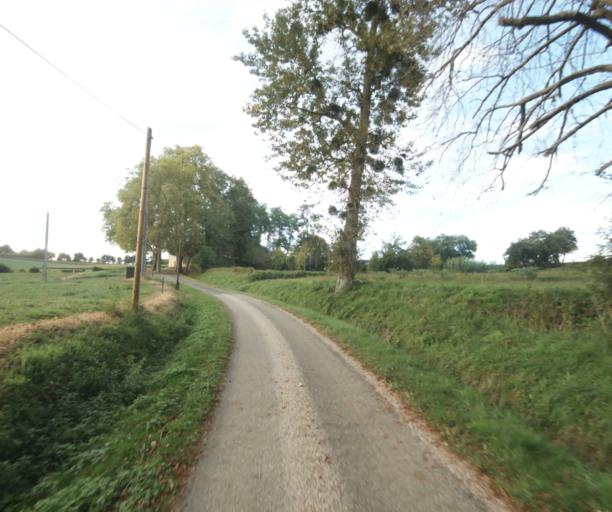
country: FR
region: Midi-Pyrenees
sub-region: Departement du Gers
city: Le Houga
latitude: 43.8505
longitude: -0.1434
